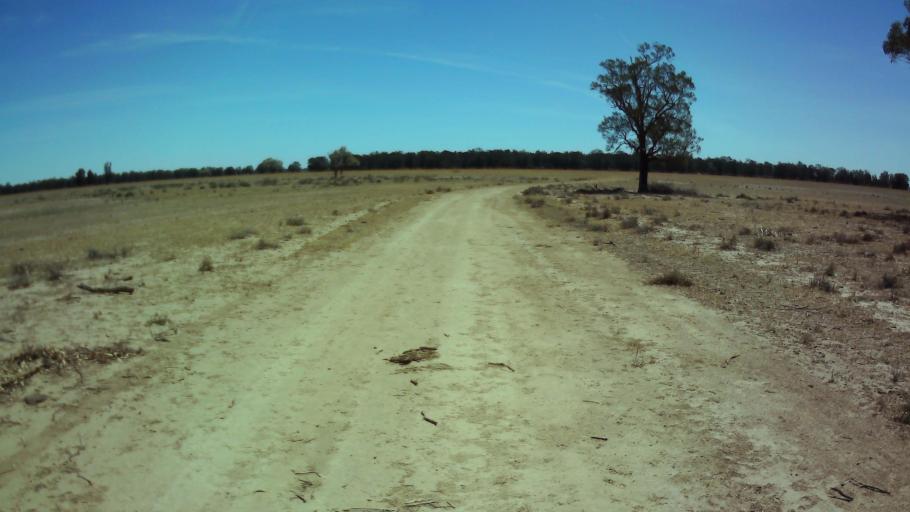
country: AU
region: New South Wales
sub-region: Bland
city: West Wyalong
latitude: -33.8383
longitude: 147.6322
